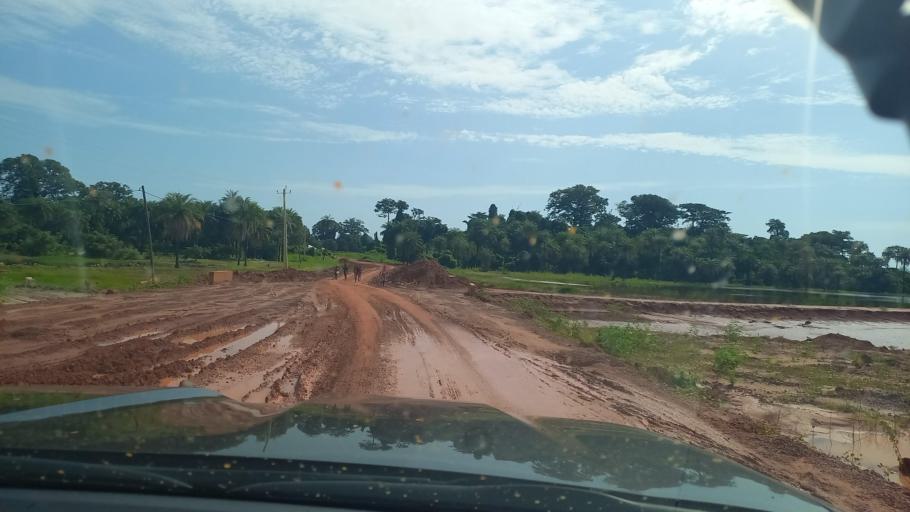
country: SN
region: Ziguinchor
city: Ziguinchor
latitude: 12.6740
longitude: -16.2017
